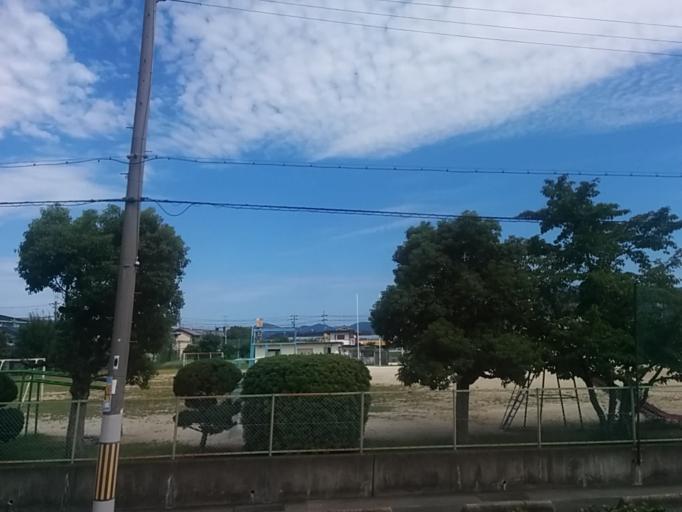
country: JP
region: Nara
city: Kashihara-shi
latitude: 34.4975
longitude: 135.7942
